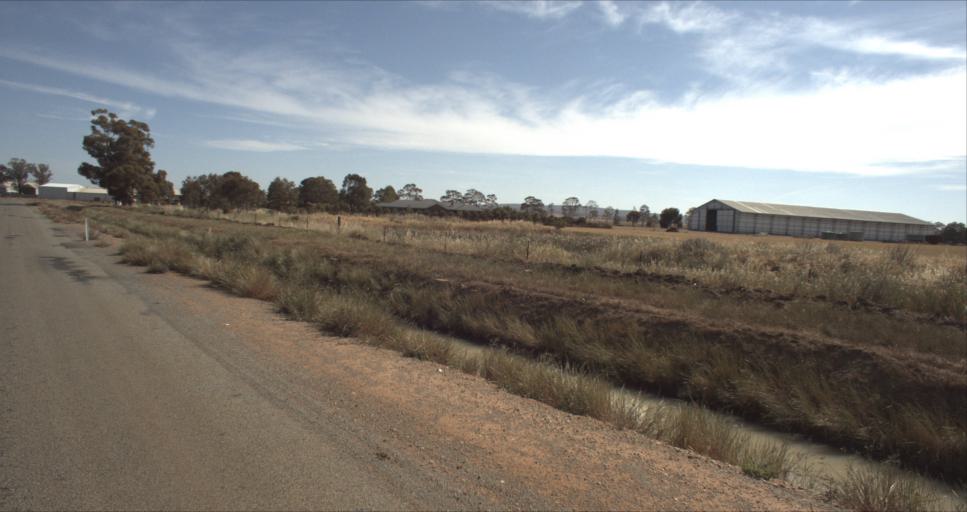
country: AU
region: New South Wales
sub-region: Leeton
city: Leeton
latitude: -34.5610
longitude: 146.4688
